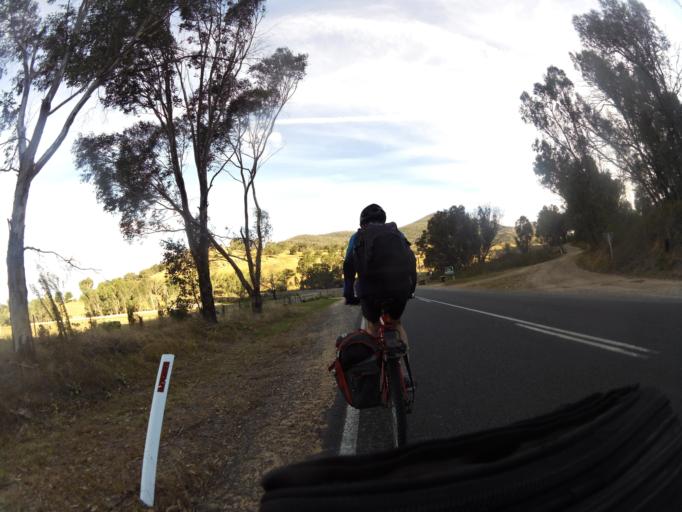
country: AU
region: New South Wales
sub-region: Greater Hume Shire
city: Holbrook
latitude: -36.0004
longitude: 147.8697
